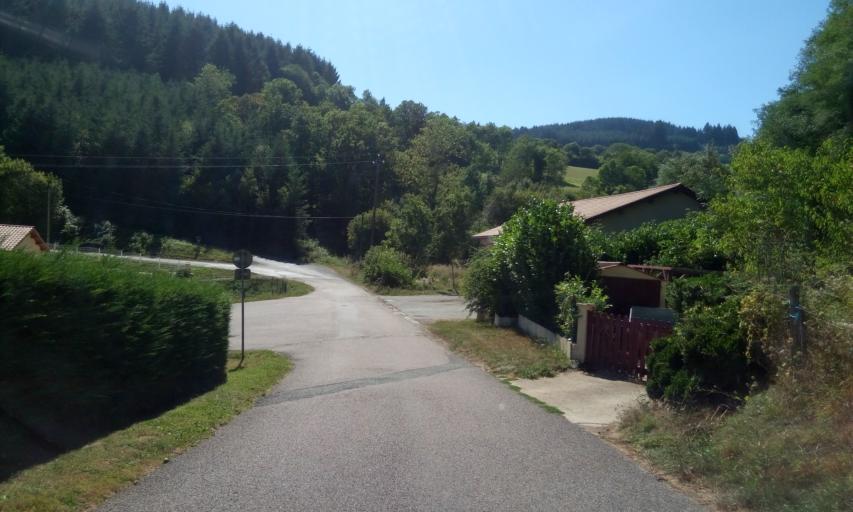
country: FR
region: Rhone-Alpes
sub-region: Departement du Rhone
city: Grandris
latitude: 46.0014
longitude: 4.4423
